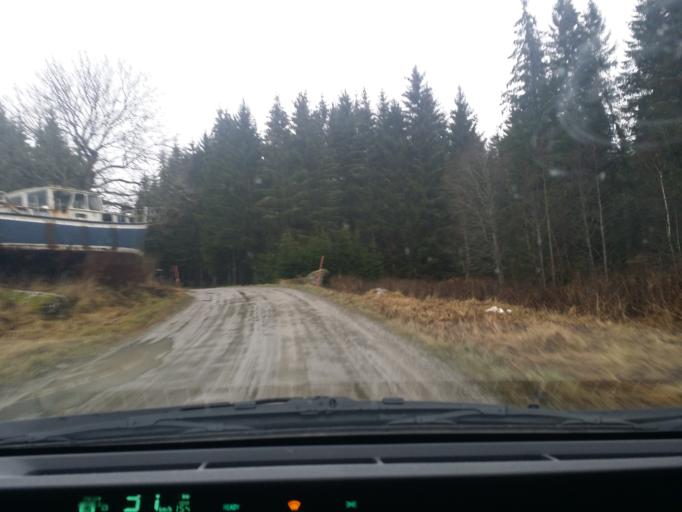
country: SE
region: Vaestmanland
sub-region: Vasteras
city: Skultuna
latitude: 59.7715
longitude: 16.3233
